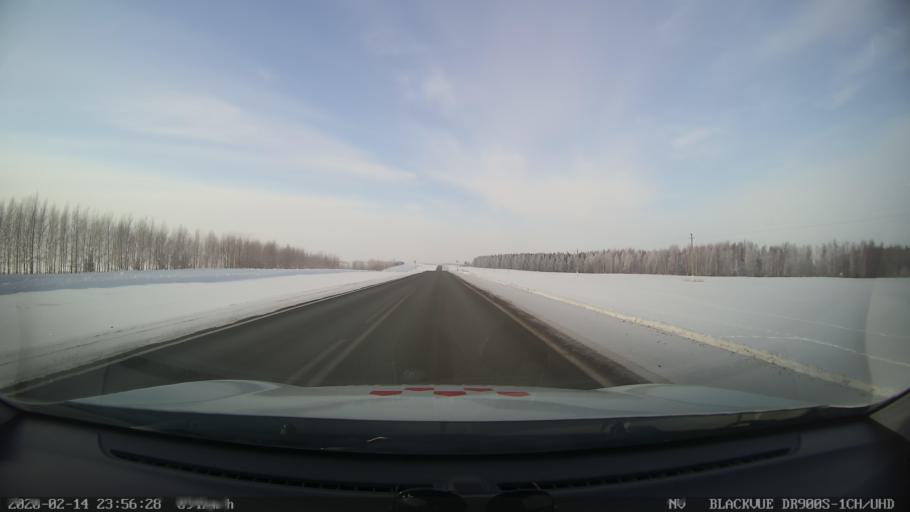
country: RU
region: Tatarstan
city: Kuybyshevskiy Zaton
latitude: 55.3249
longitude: 49.1296
